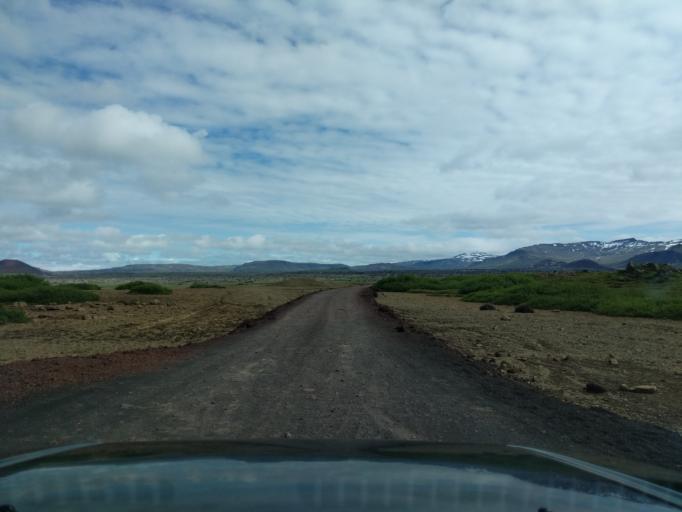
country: IS
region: West
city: Stykkisholmur
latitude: 64.8334
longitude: -22.3158
